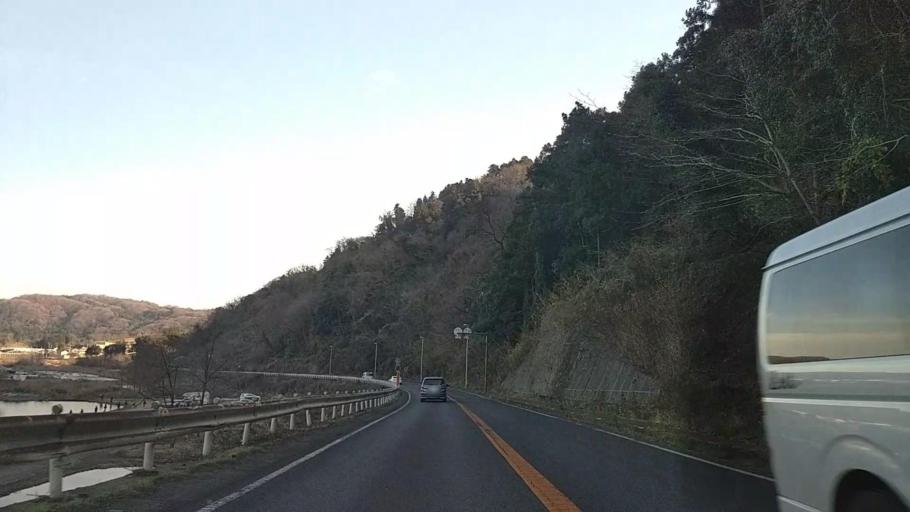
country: JP
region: Kanagawa
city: Zama
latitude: 35.5239
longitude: 139.2829
